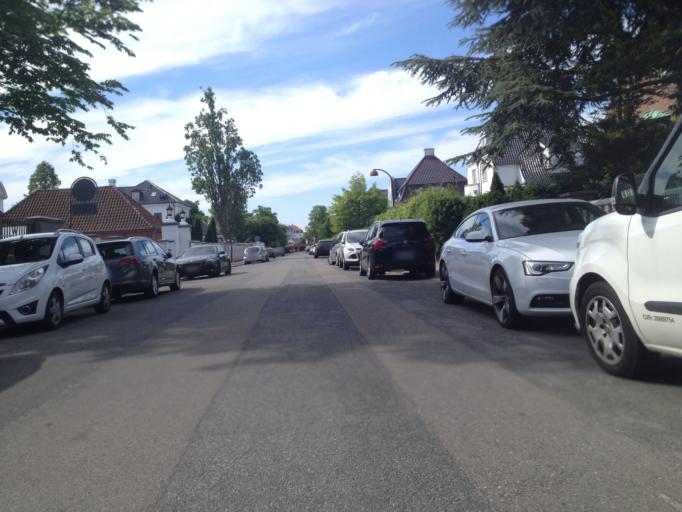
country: DK
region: Capital Region
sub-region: Gentofte Kommune
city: Charlottenlund
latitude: 55.7388
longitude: 12.5825
